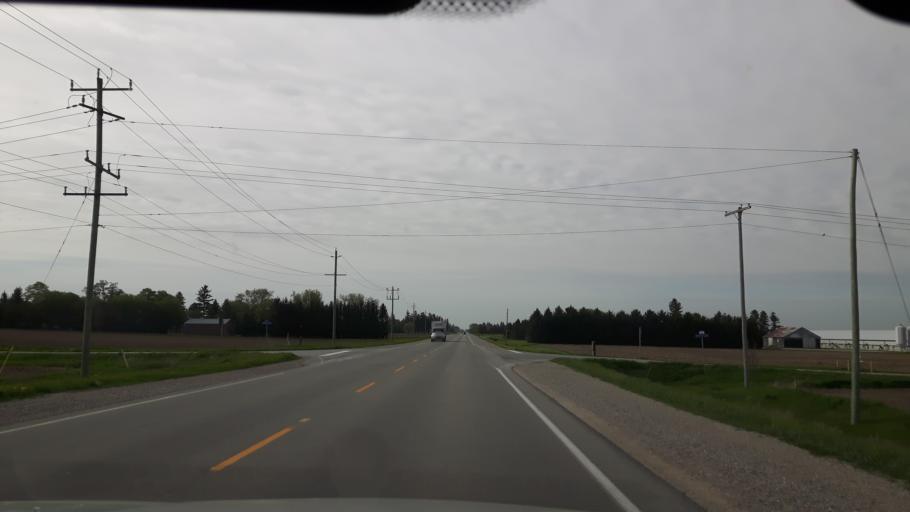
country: CA
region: Ontario
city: South Huron
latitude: 43.3987
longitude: -81.4913
